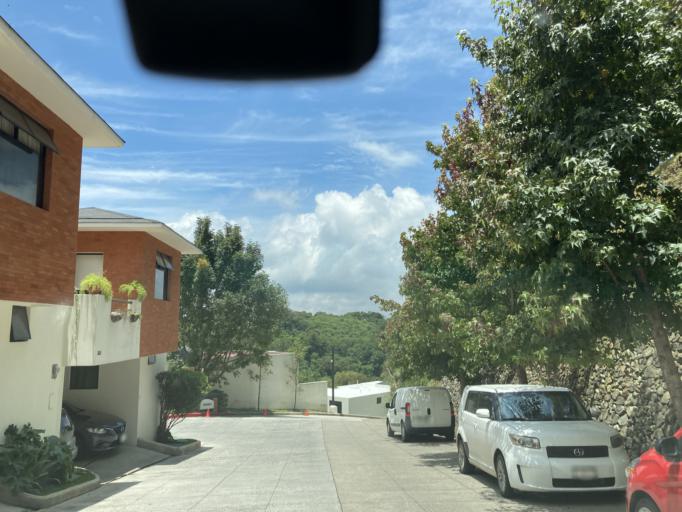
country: GT
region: Guatemala
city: Fraijanes
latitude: 14.5068
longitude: -90.4603
